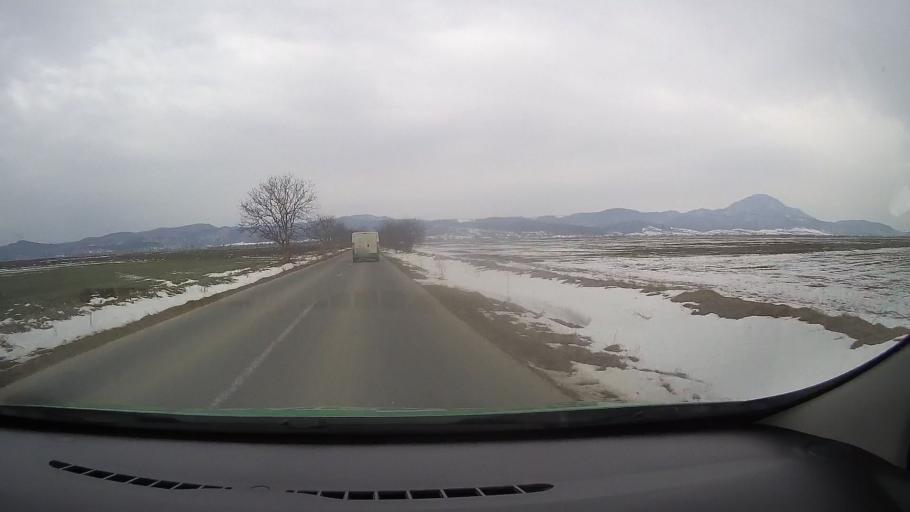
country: RO
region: Brasov
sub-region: Comuna Cristian
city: Cristian
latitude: 45.6343
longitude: 25.4527
